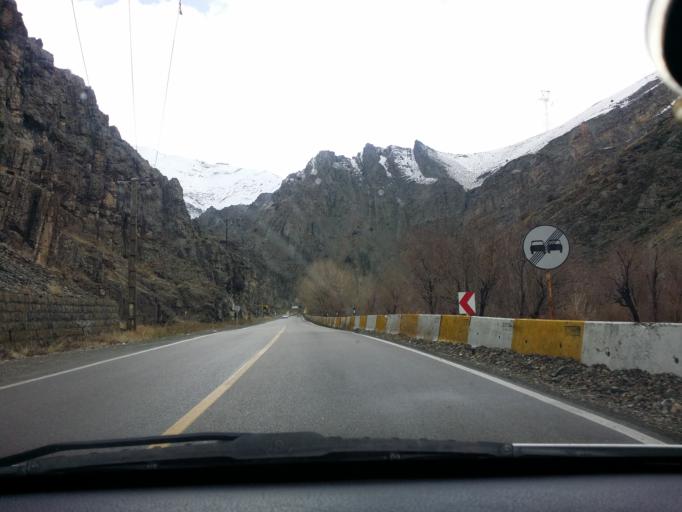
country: IR
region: Tehran
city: Tajrish
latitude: 36.0146
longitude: 51.2864
